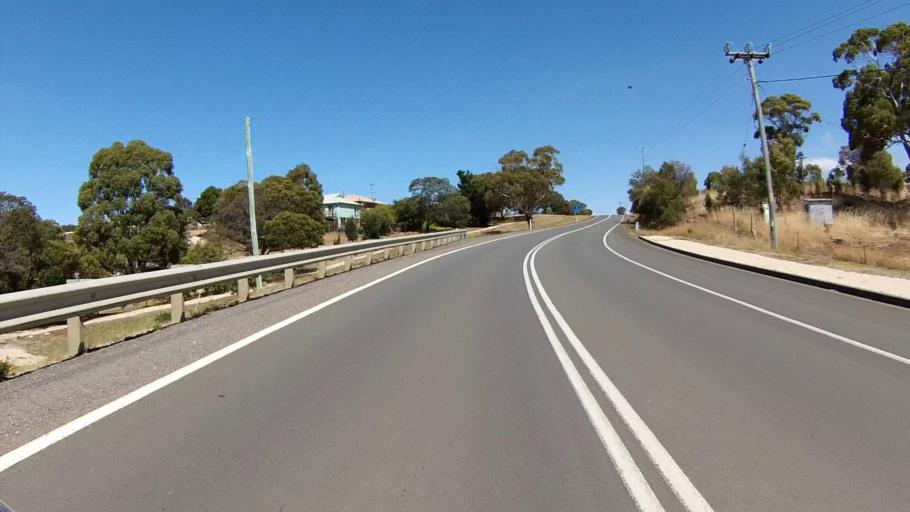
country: AU
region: Tasmania
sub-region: Sorell
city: Sorell
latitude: -42.1310
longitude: 148.0725
